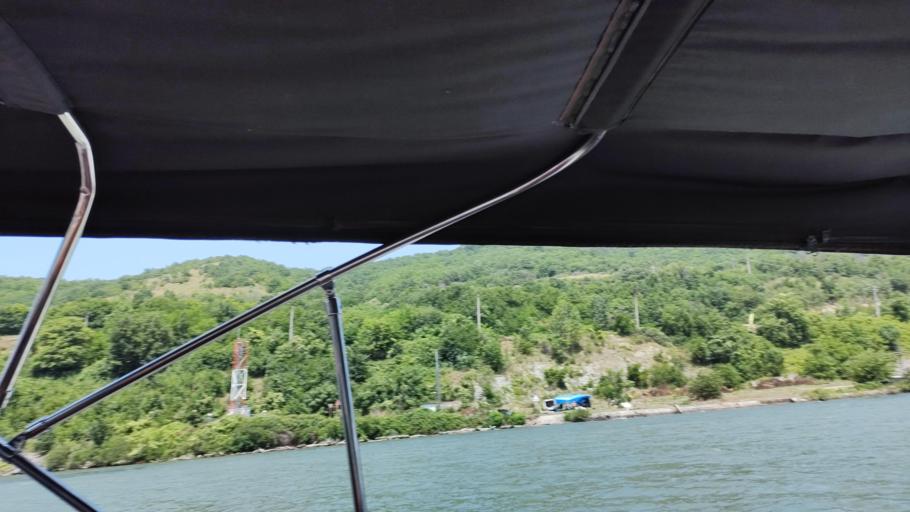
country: RO
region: Caras-Severin
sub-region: Comuna Berzasca
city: Berzasca
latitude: 44.6365
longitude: 21.9630
